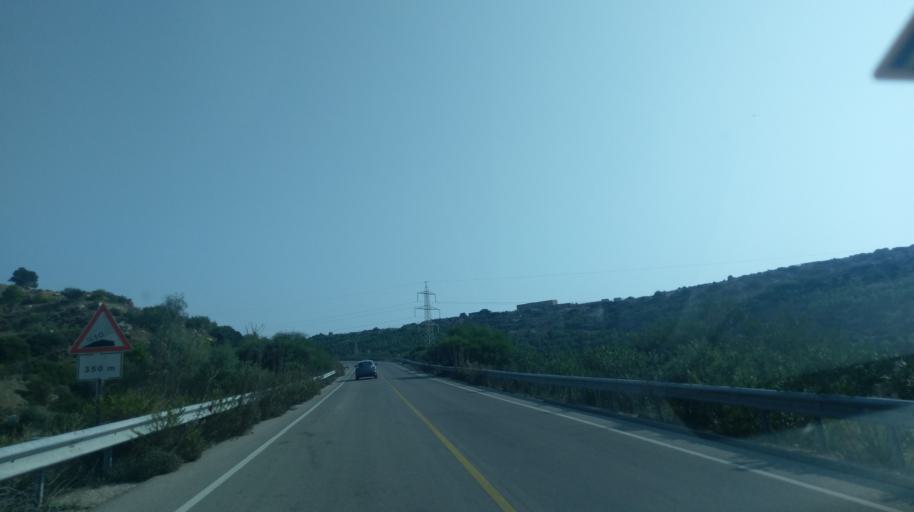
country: CY
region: Ammochostos
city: Leonarisso
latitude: 35.4772
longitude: 34.1349
